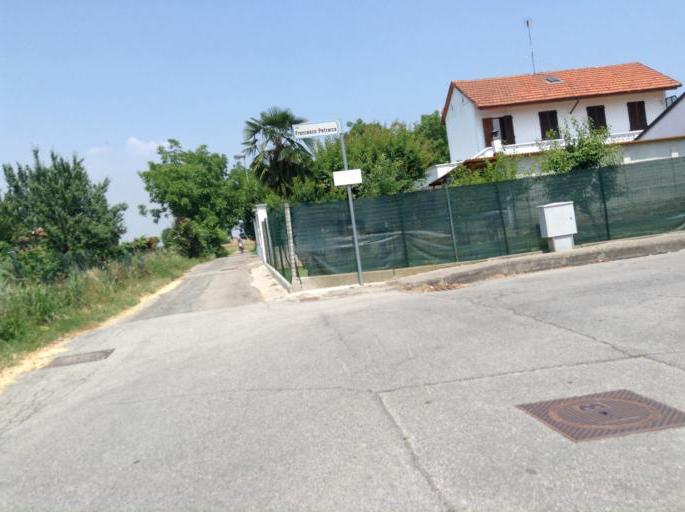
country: IT
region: Piedmont
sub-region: Provincia di Torino
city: Carignano
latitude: 44.9135
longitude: 7.6732
